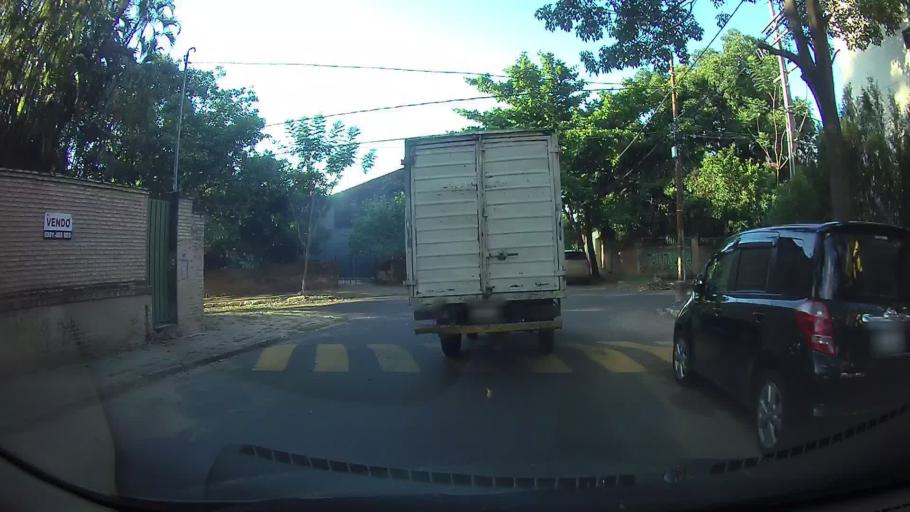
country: PY
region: Asuncion
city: Asuncion
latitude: -25.2787
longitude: -57.6056
